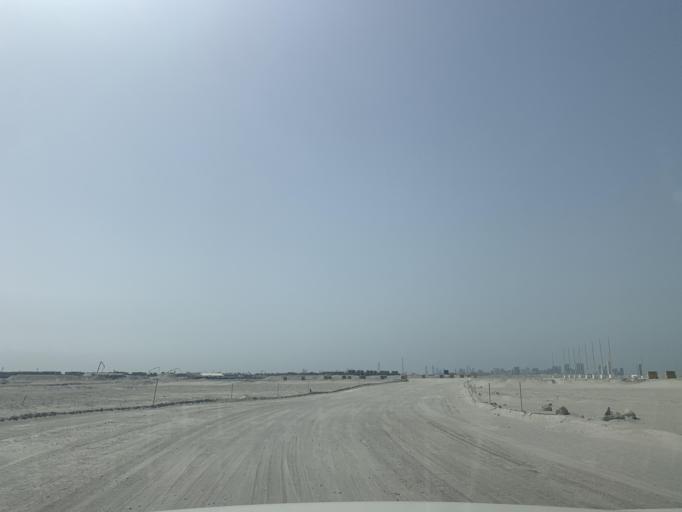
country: BH
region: Northern
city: Sitrah
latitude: 26.1601
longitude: 50.6423
